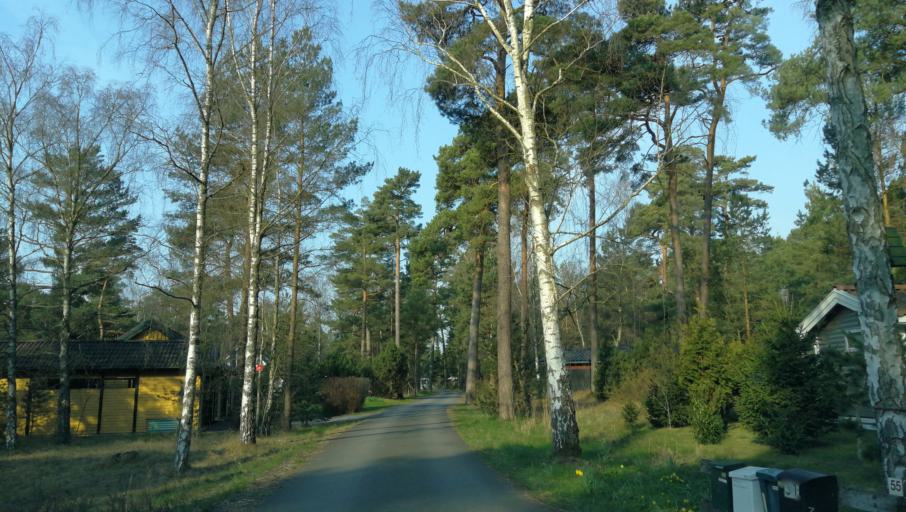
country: SE
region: Skane
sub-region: Ystads Kommun
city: Kopingebro
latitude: 55.4363
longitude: 13.8840
